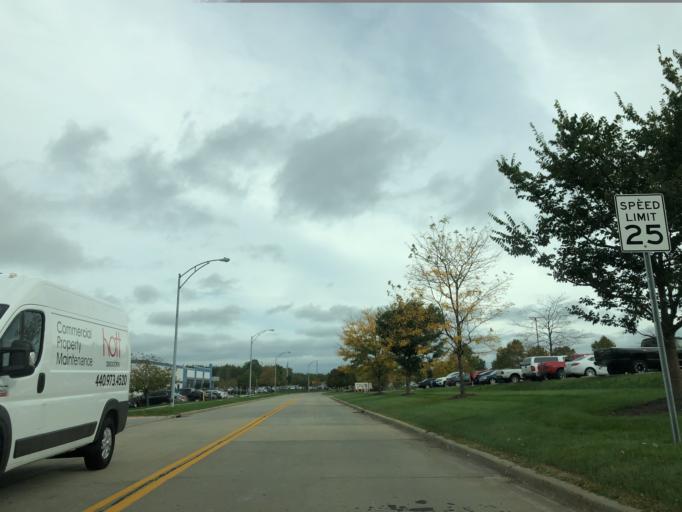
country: US
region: Ohio
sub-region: Cuyahoga County
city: Brecksville
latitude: 41.2862
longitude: -81.6341
